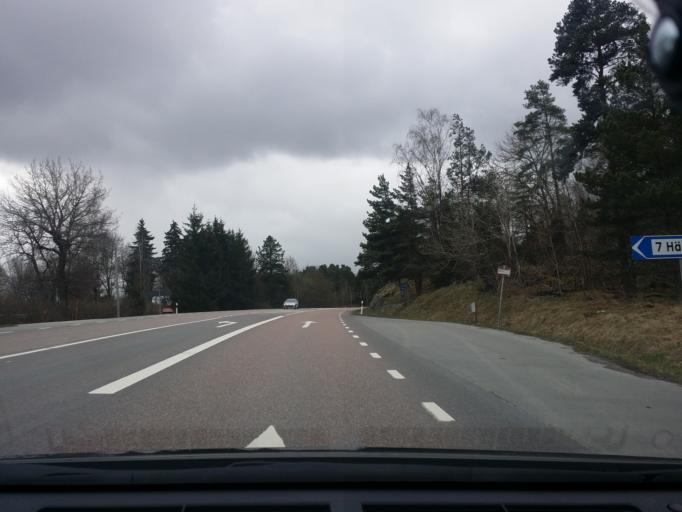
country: SE
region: Uppsala
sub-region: Enkopings Kommun
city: Irsta
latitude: 59.7331
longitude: 16.9573
